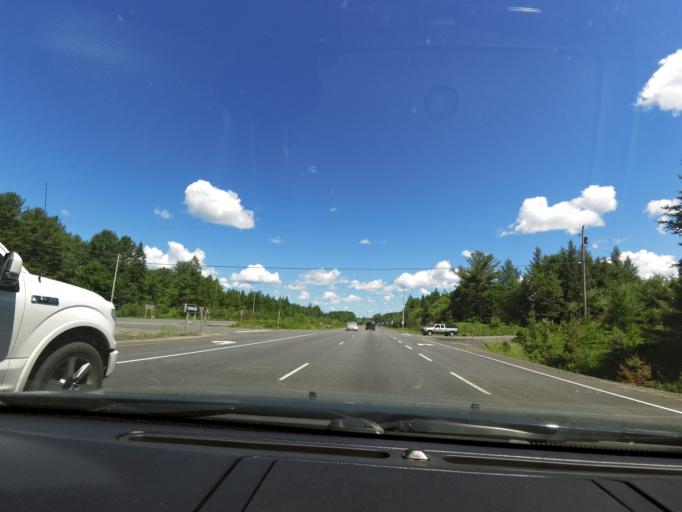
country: CA
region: Ontario
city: Bracebridge
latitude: 45.1763
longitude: -79.3118
